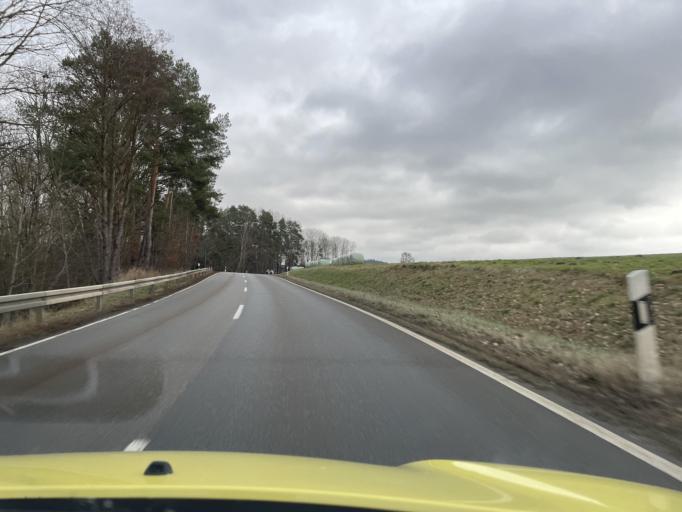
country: DE
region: Bavaria
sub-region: Upper Palatinate
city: Zandt
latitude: 49.1674
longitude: 12.7072
